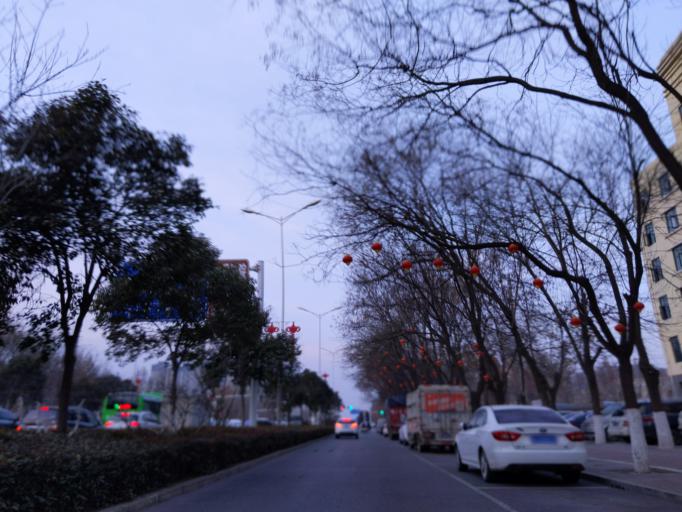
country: CN
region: Henan Sheng
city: Puyang
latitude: 35.7798
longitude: 115.0207
